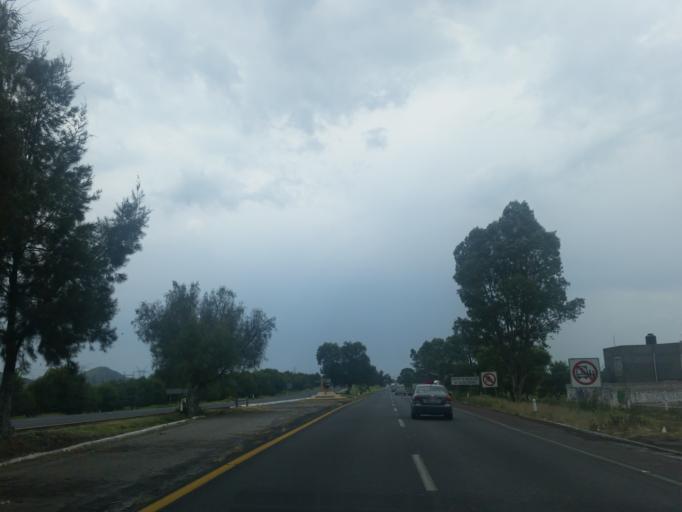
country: MX
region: Morelos
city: Teotihuacan de Arista
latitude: 19.6779
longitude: -98.8613
